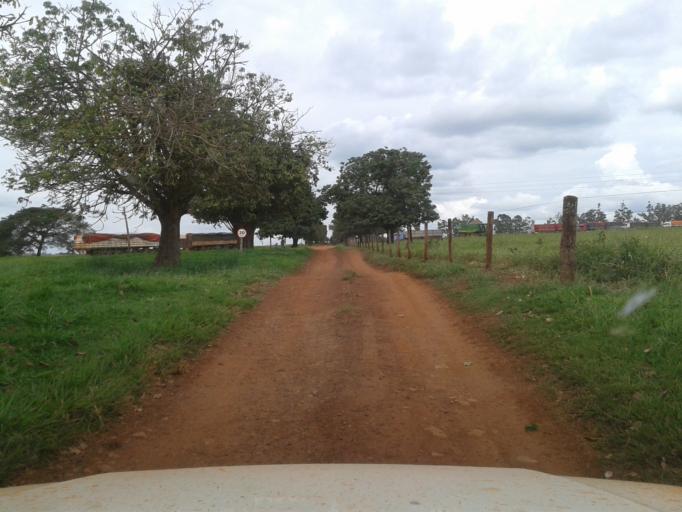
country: BR
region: Minas Gerais
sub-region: Centralina
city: Centralina
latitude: -18.7738
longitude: -49.2266
